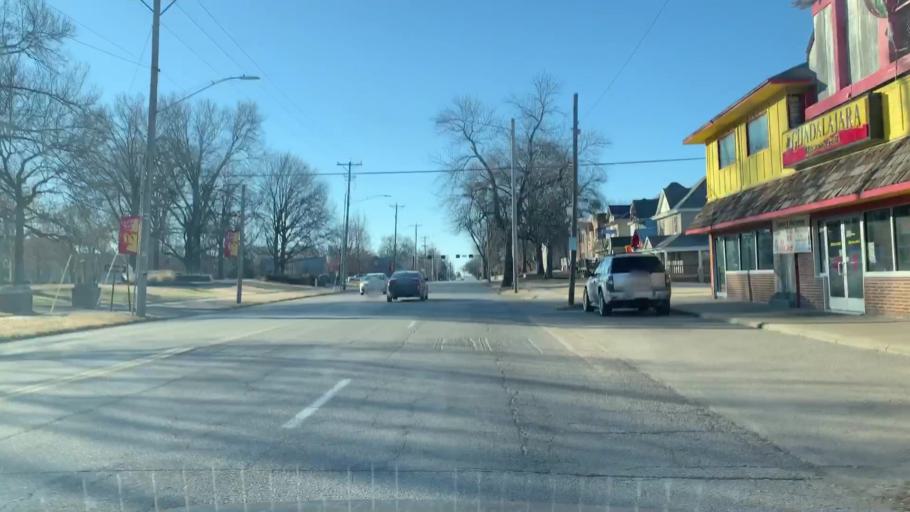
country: US
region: Kansas
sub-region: Crawford County
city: Pittsburg
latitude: 37.3922
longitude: -94.7051
